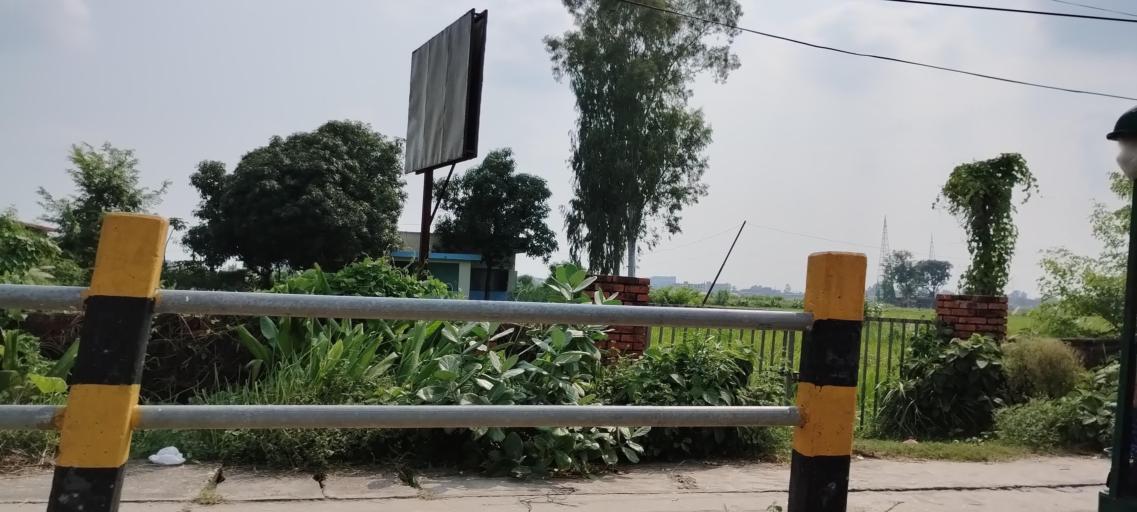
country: NP
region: Mid Western
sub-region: Bheri Zone
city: Nepalgunj
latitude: 28.0986
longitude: 81.6598
